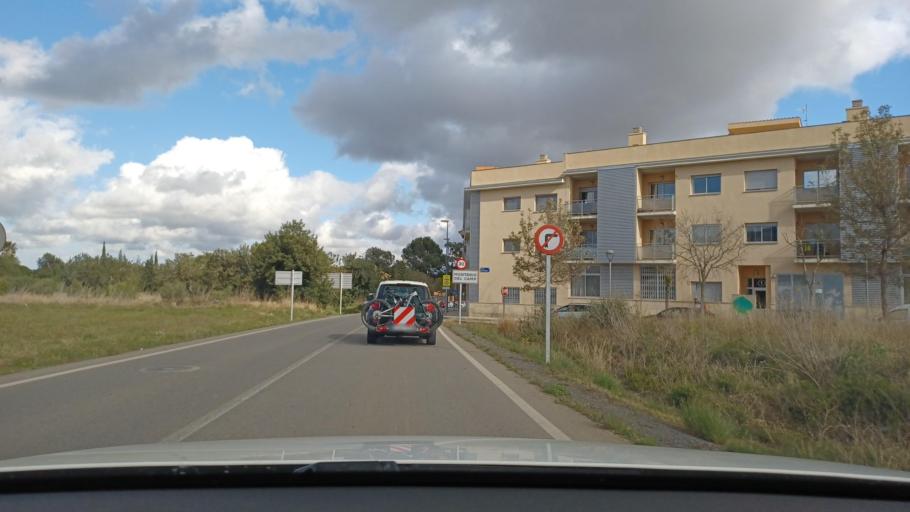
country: ES
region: Catalonia
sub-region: Provincia de Tarragona
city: Botarell
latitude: 41.1239
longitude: 0.9991
